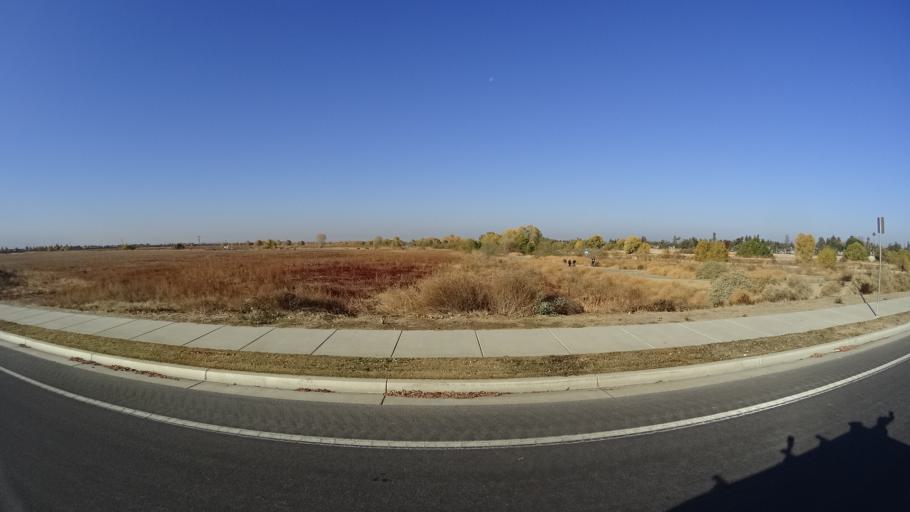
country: US
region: California
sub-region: Kern County
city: Rosedale
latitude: 35.3447
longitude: -119.1456
